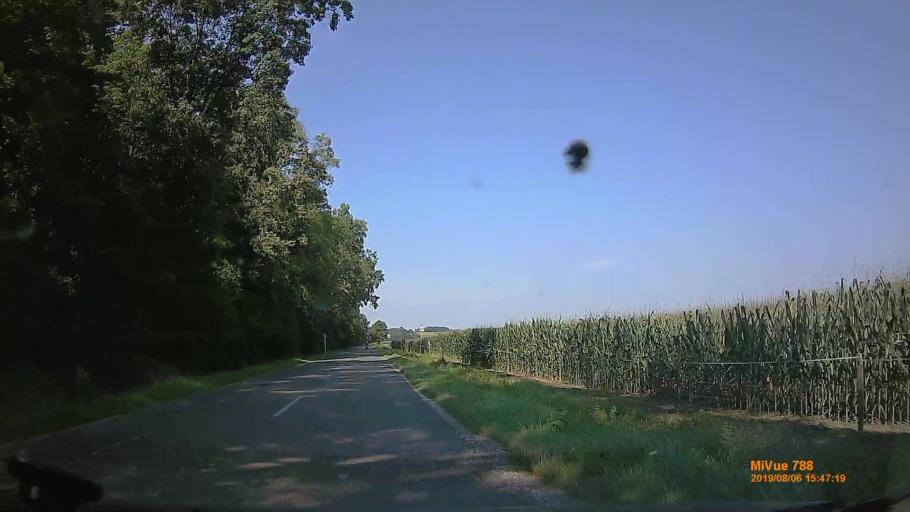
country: HU
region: Somogy
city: Csurgo
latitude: 46.2562
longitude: 17.0241
